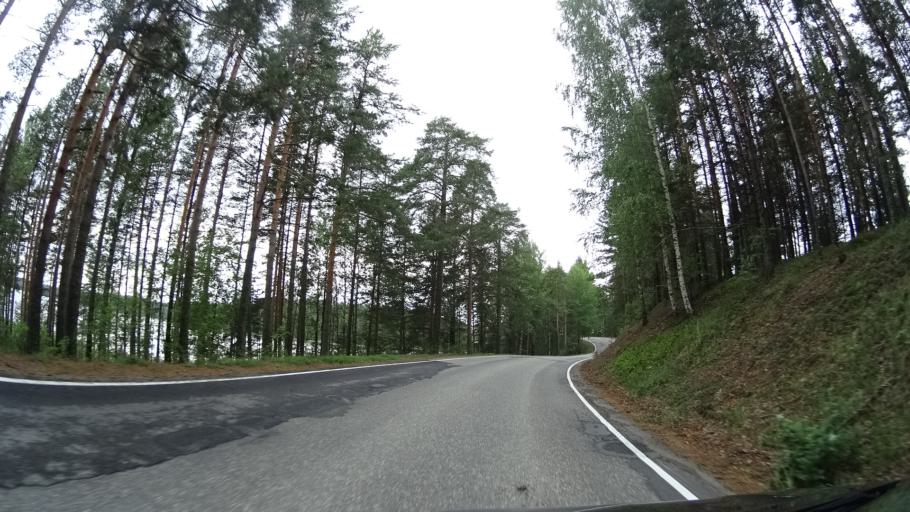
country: FI
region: Southern Savonia
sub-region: Savonlinna
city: Punkaharju
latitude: 61.7537
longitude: 29.4261
